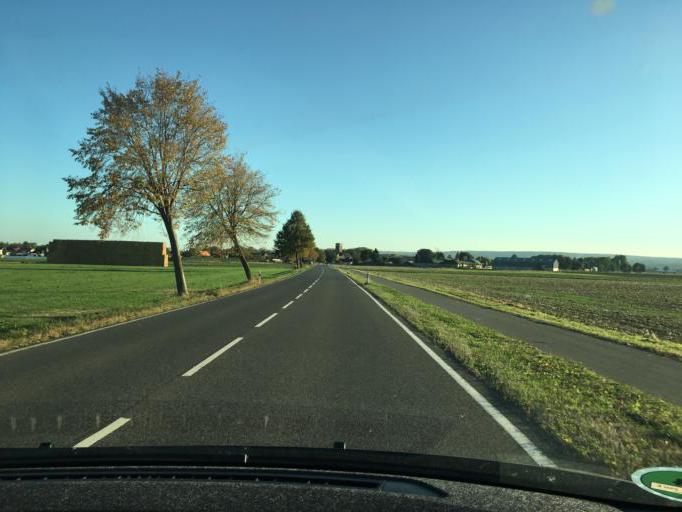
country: DE
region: North Rhine-Westphalia
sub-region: Regierungsbezirk Koln
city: Inden
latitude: 50.8337
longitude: 6.4164
